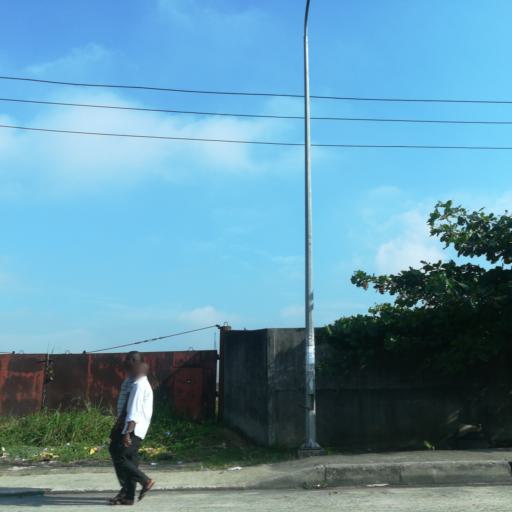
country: NG
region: Rivers
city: Port Harcourt
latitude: 4.8015
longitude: 7.0257
